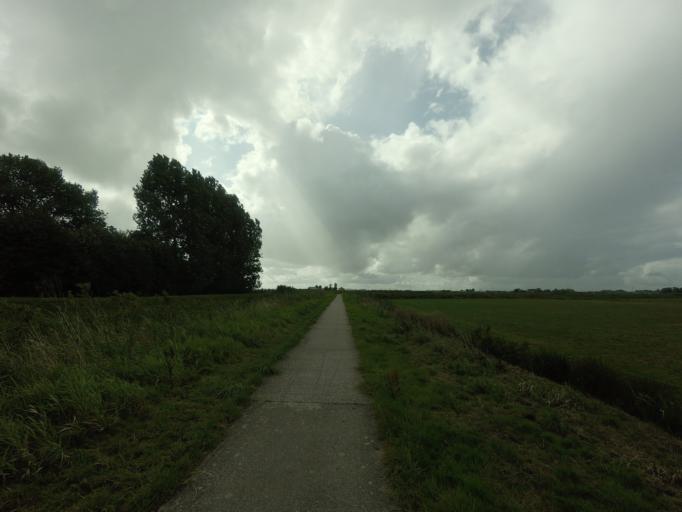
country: NL
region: Friesland
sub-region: Gemeente Leeuwarden
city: Wirdum
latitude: 53.1438
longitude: 5.8241
